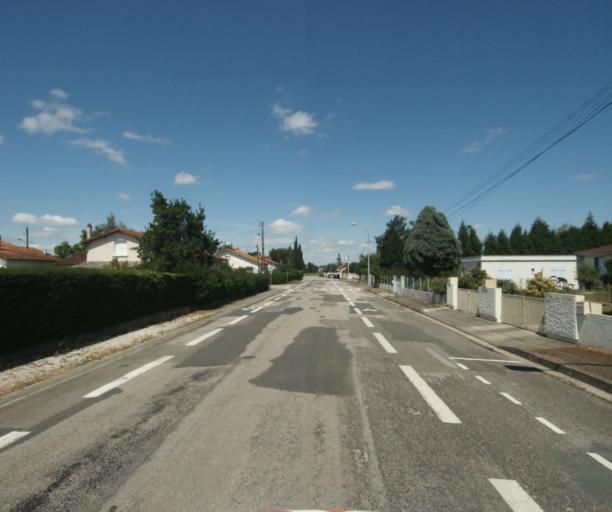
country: FR
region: Midi-Pyrenees
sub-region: Departement de la Haute-Garonne
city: Revel
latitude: 43.4580
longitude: 2.0137
